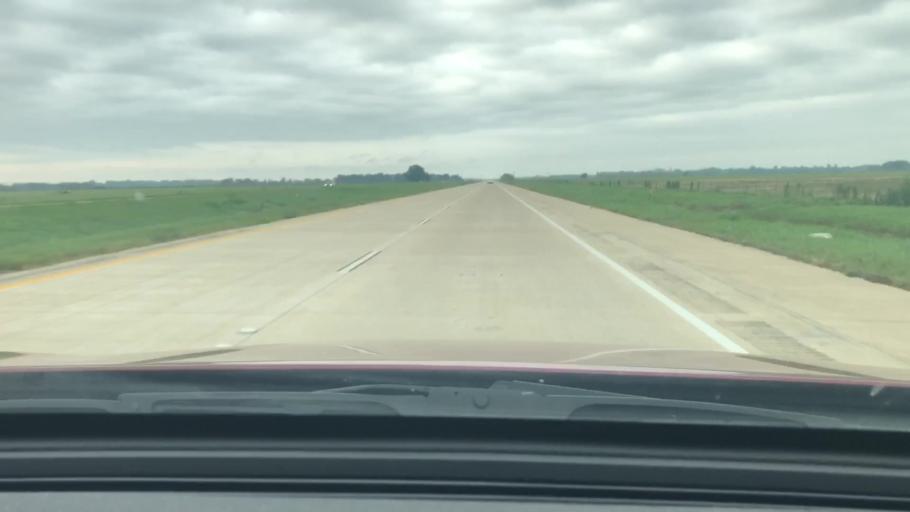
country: US
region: Louisiana
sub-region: Caddo Parish
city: Oil City
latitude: 32.7374
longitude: -93.8765
